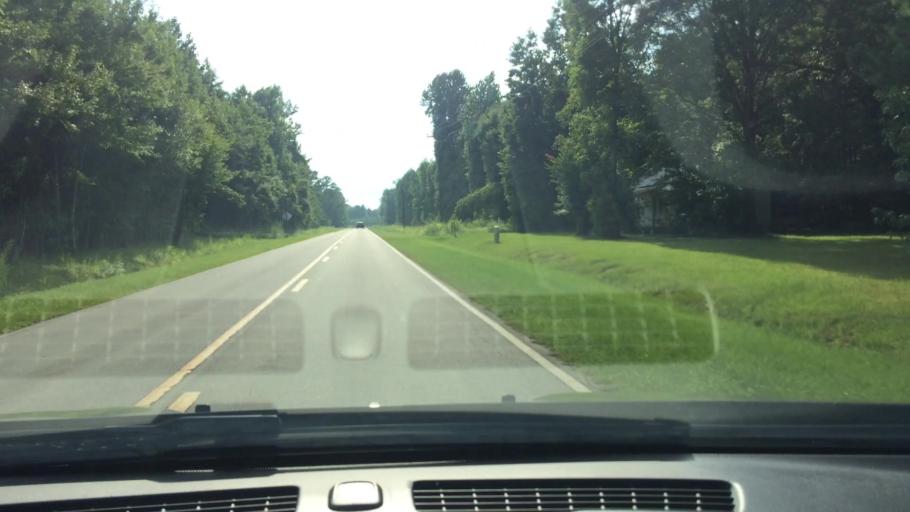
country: US
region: North Carolina
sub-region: Beaufort County
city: River Road
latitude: 35.4360
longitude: -76.9876
